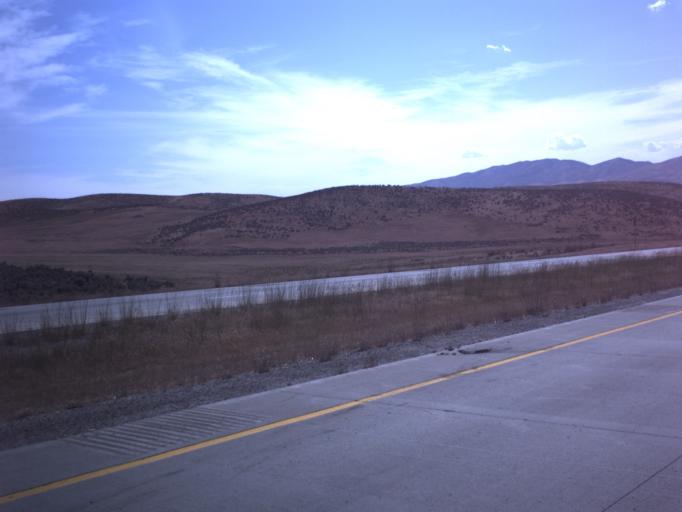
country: US
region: Utah
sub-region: Box Elder County
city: Garland
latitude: 41.8159
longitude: -112.3654
